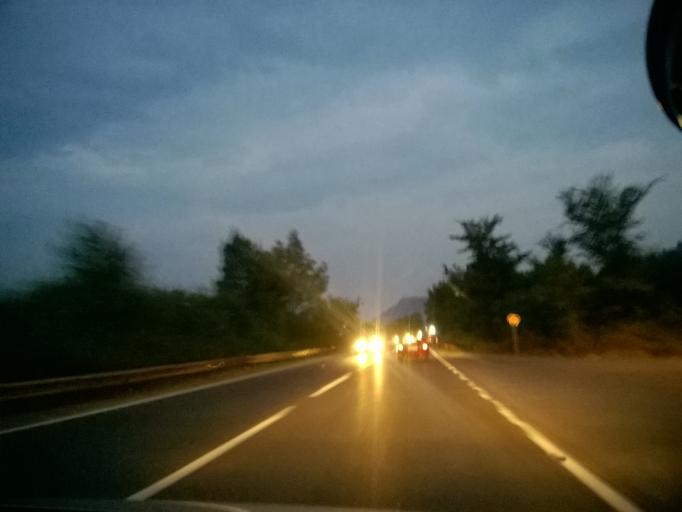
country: ME
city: Spuz
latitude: 42.4829
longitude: 19.1665
